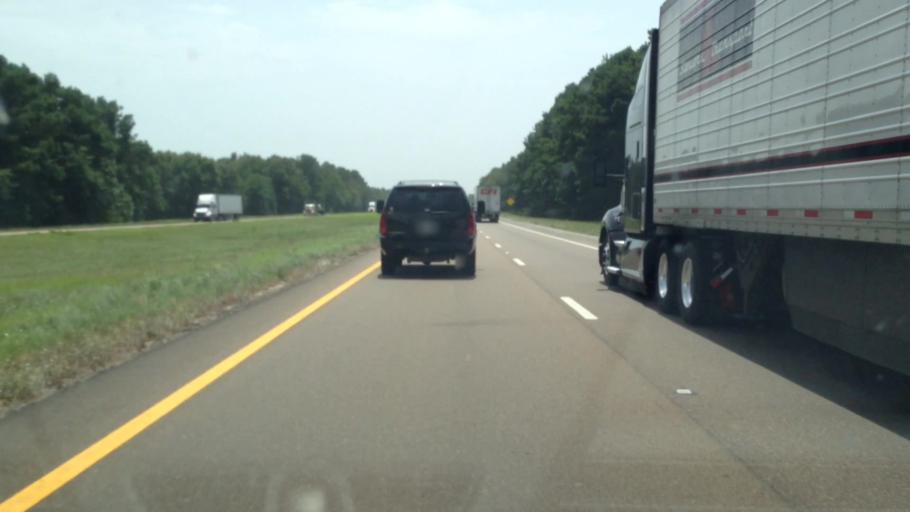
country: US
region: Texas
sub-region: Morris County
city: Omaha
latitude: 33.2824
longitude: -94.7951
